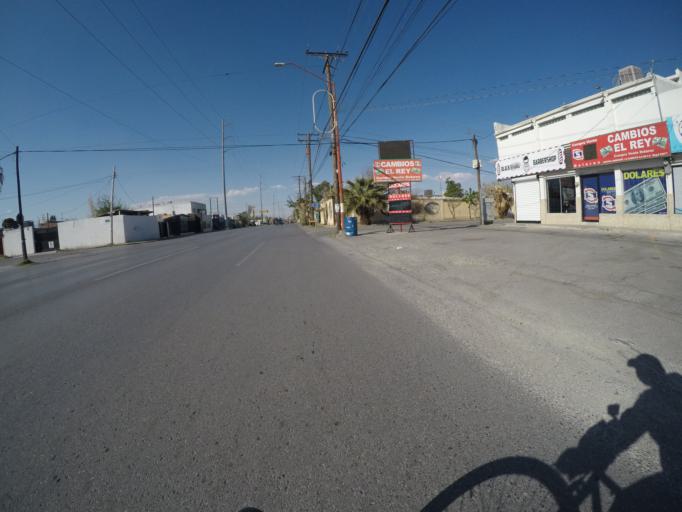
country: MX
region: Chihuahua
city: Ciudad Juarez
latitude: 31.7265
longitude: -106.4420
